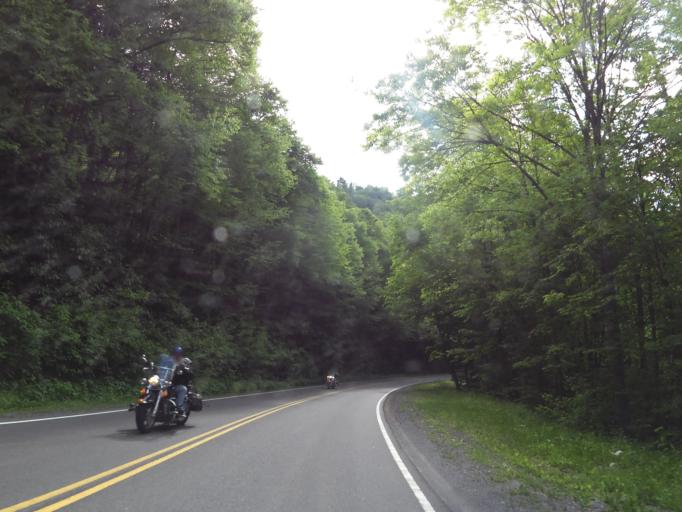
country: US
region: Tennessee
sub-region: Sevier County
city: Gatlinburg
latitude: 35.6308
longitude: -83.4589
